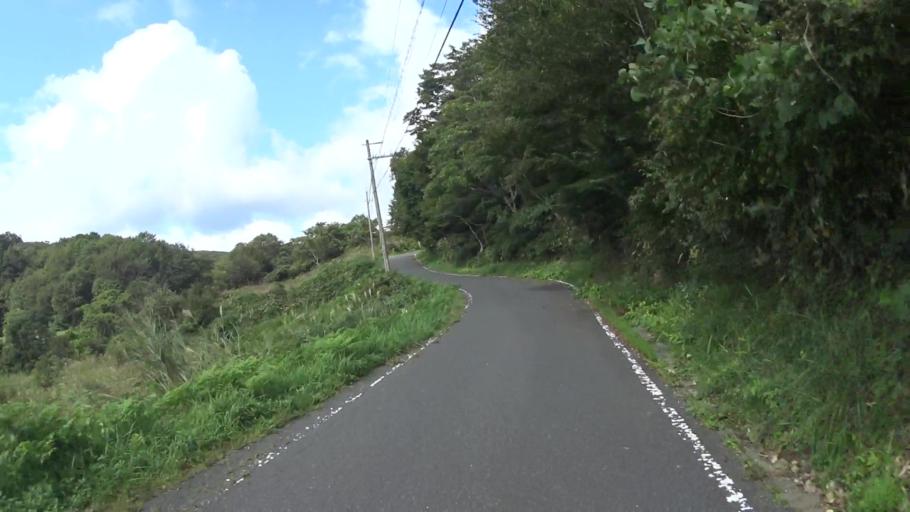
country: JP
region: Kyoto
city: Miyazu
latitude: 35.6453
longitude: 135.1827
